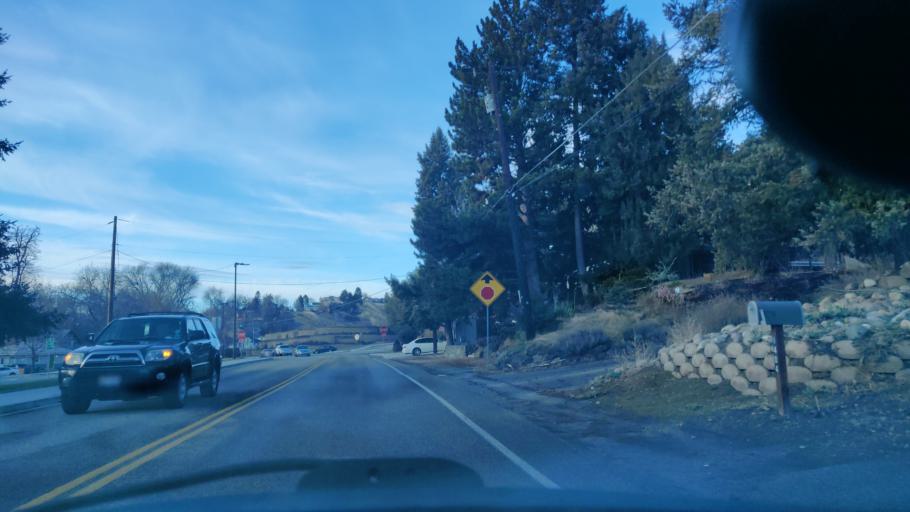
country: US
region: Idaho
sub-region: Ada County
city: Boise
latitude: 43.6383
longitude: -116.2052
